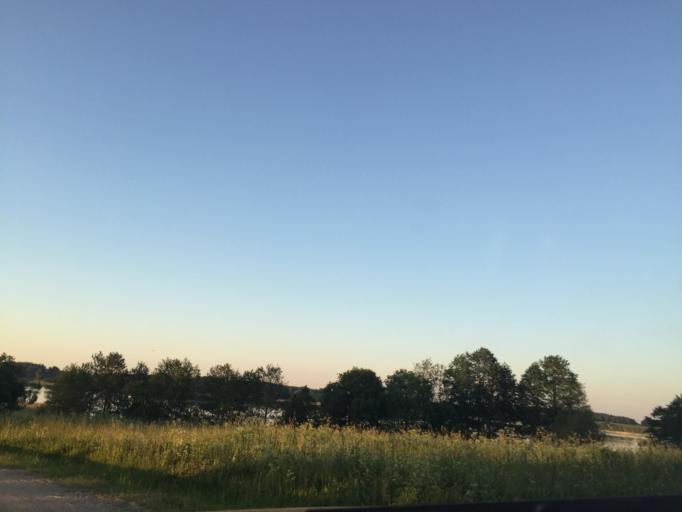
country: LV
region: Rezekne
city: Rezekne
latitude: 56.3628
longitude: 27.4156
